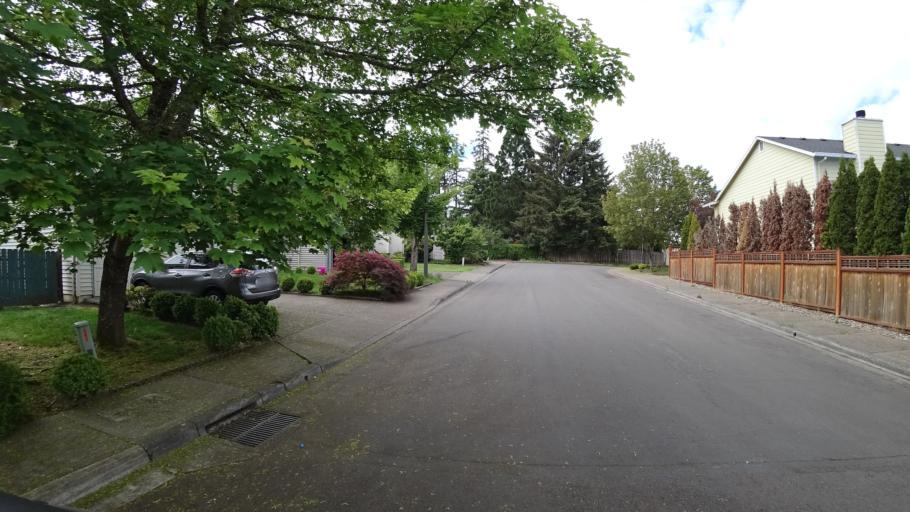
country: US
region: Oregon
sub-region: Washington County
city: Aloha
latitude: 45.4674
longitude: -122.8583
